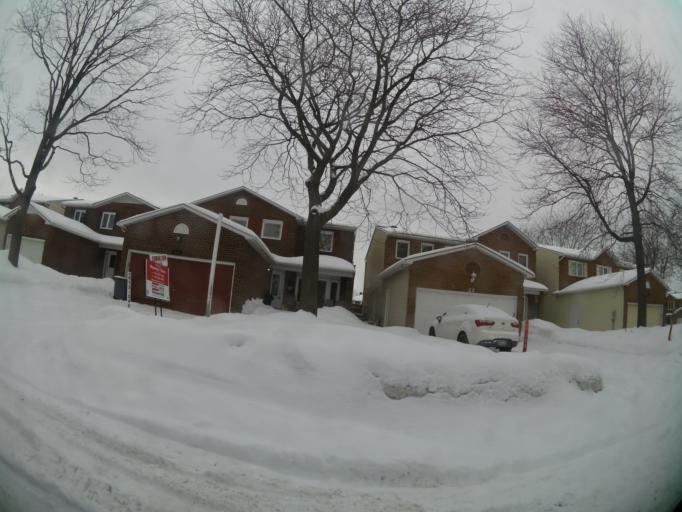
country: CA
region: Ontario
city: Ottawa
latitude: 45.3712
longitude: -75.6142
